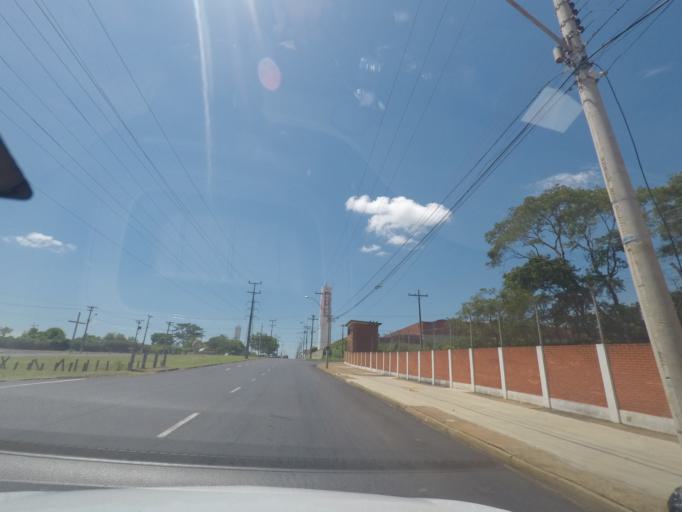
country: BR
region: Sao Paulo
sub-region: Matao
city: Matao
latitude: -21.6123
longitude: -48.3738
